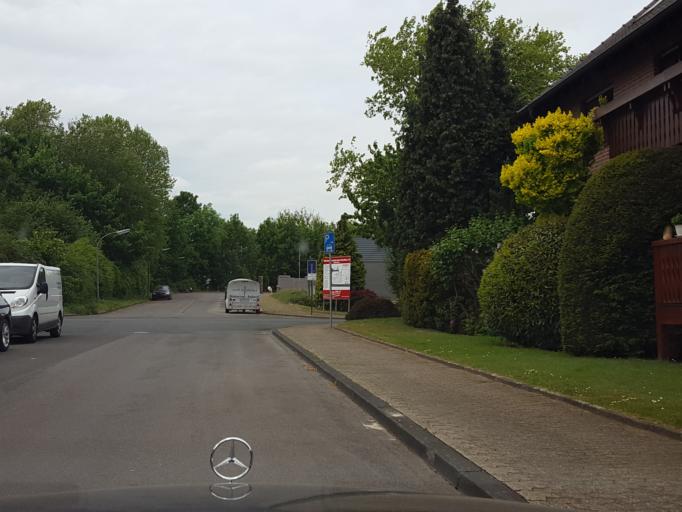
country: DE
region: North Rhine-Westphalia
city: Oer-Erkenschwick
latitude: 51.6469
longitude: 7.2820
